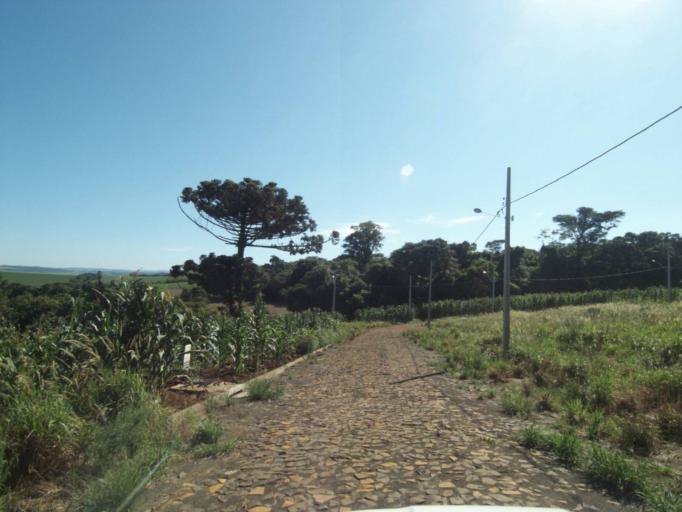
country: BR
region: Parana
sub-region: Laranjeiras Do Sul
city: Laranjeiras do Sul
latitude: -25.4848
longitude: -52.5272
